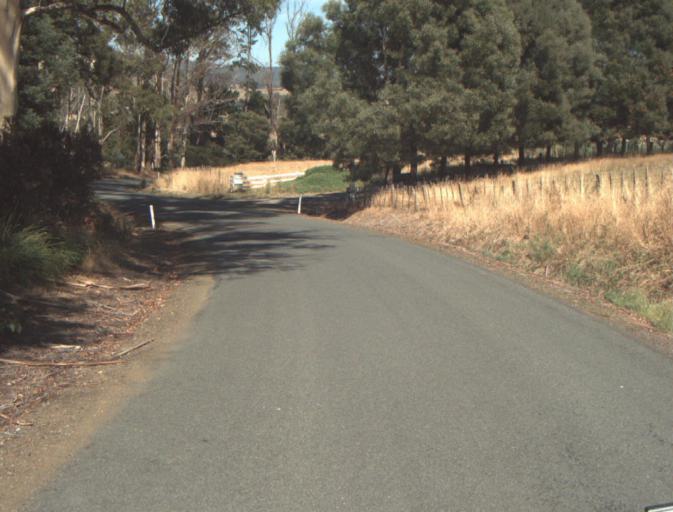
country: AU
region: Tasmania
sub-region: Launceston
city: Mayfield
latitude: -41.2397
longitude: 147.2220
